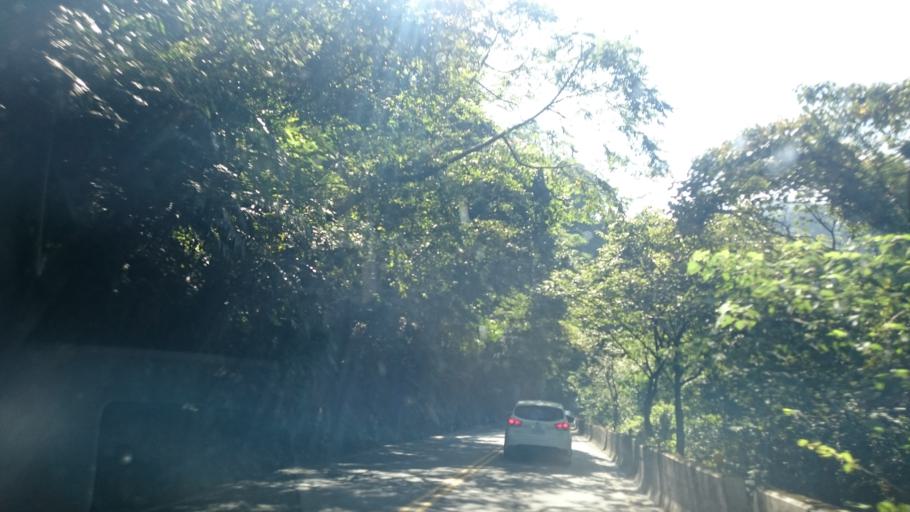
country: TW
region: Taiwan
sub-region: Nantou
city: Puli
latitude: 24.0086
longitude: 121.1086
